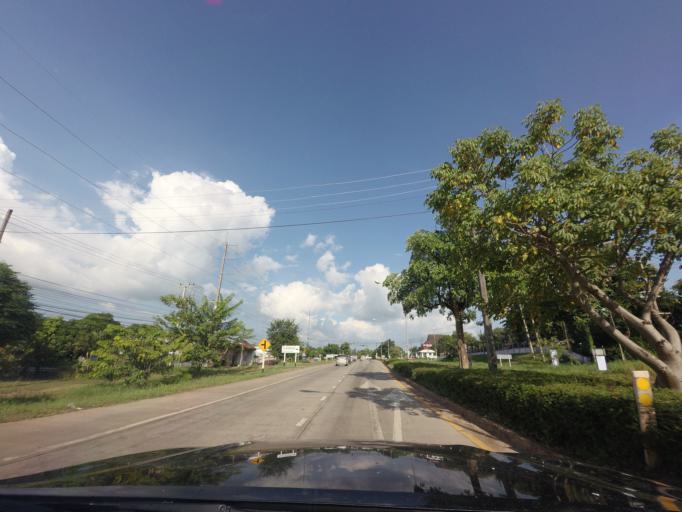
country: TH
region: Nong Khai
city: Nong Khai
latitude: 17.8876
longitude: 102.7675
